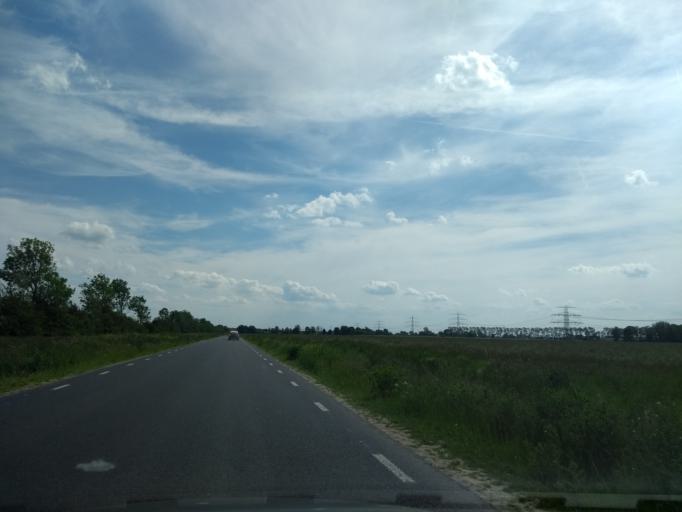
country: NL
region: Groningen
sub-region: Gemeente Zuidhorn
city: Aduard
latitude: 53.2558
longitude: 6.4811
